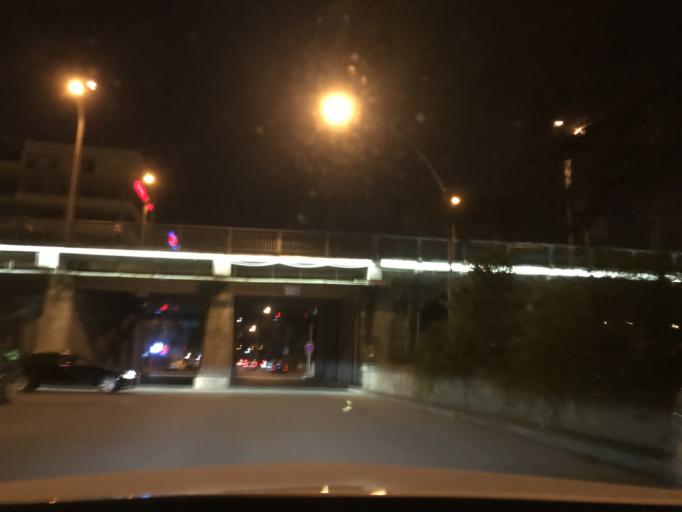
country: CN
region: Sichuan
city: Mianyang
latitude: 31.4486
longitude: 104.7516
